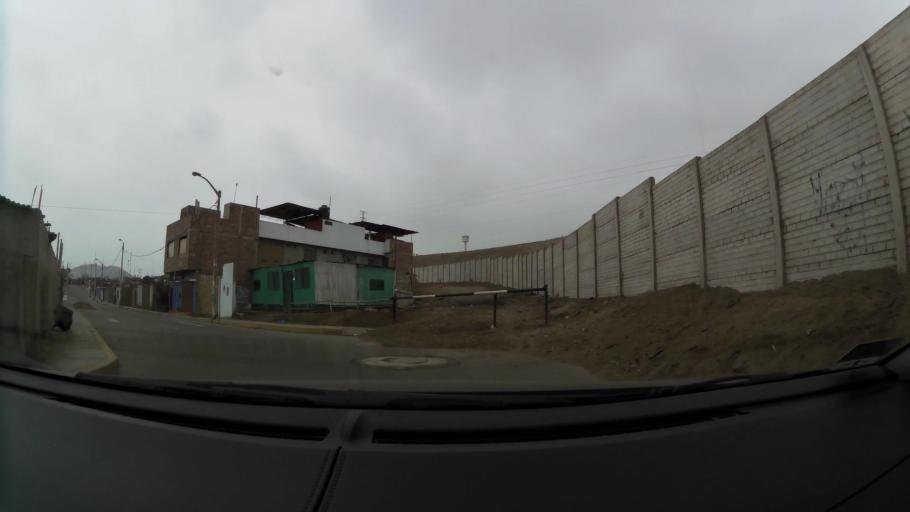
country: PE
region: Lima
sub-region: Provincia de Huaral
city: Chancay
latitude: -11.5972
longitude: -77.2515
